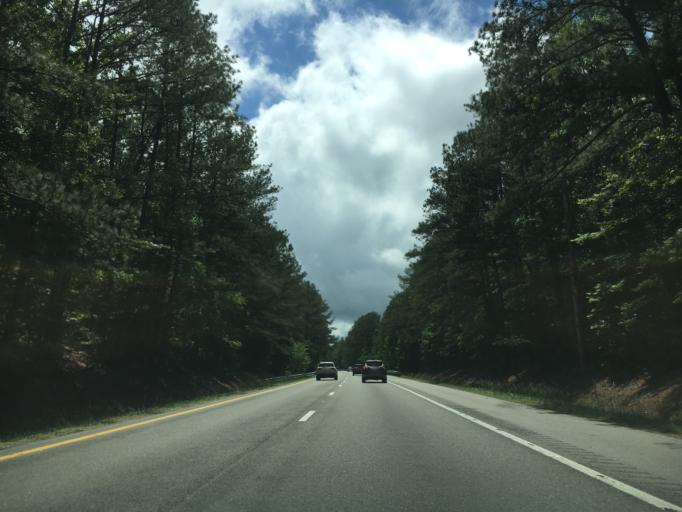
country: US
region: Virginia
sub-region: Brunswick County
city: Lawrenceville
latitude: 36.8176
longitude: -77.9683
